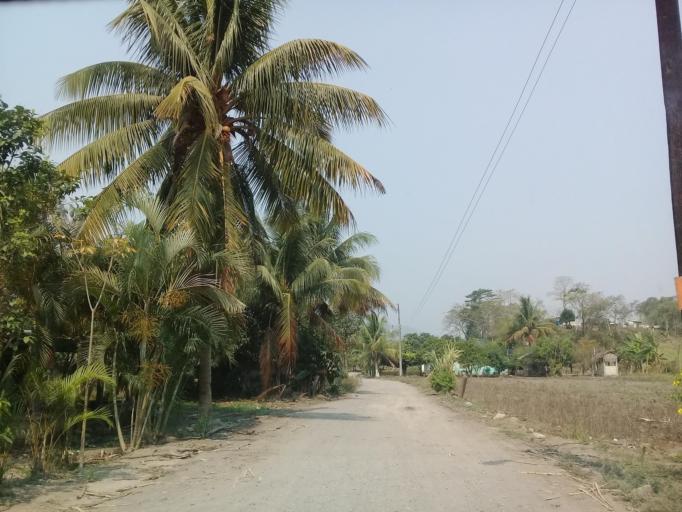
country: MX
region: Oaxaca
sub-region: Acatlan de Perez Figueroa
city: Zona Urbana Ejidal
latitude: 18.5890
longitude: -96.5595
